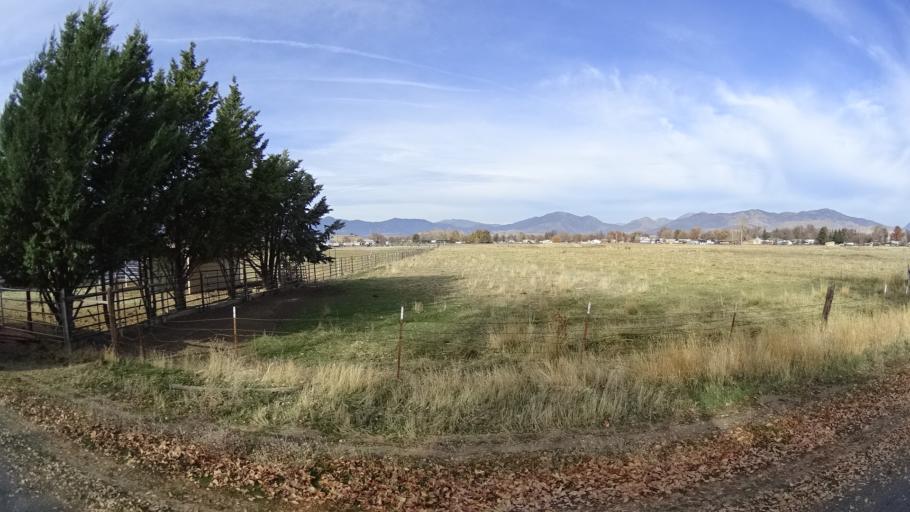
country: US
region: California
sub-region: Siskiyou County
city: Montague
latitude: 41.7216
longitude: -122.5203
